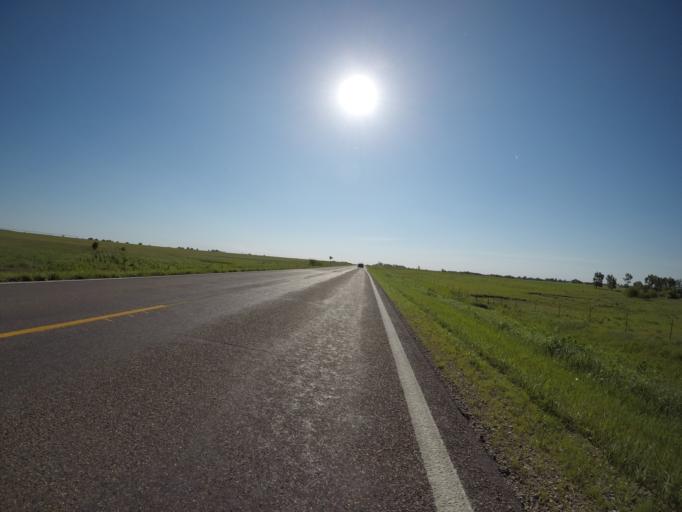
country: US
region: Kansas
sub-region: Lyon County
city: Emporia
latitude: 38.6588
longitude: -96.2149
